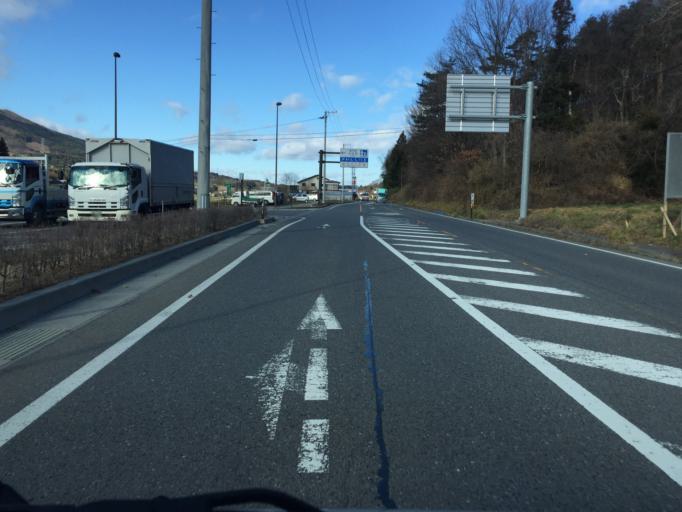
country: JP
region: Fukushima
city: Ishikawa
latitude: 37.2503
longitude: 140.5609
